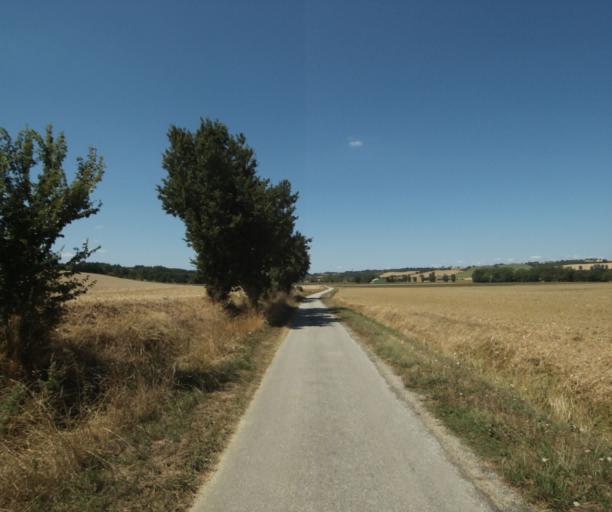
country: FR
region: Midi-Pyrenees
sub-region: Departement de la Haute-Garonne
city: Saint-Felix-Lauragais
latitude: 43.4787
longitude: 1.8779
